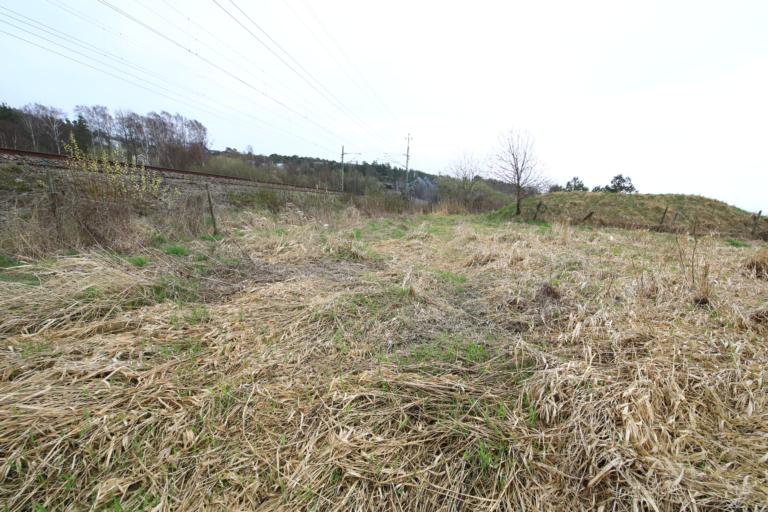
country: SE
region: Halland
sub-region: Kungsbacka Kommun
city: Frillesas
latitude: 57.3071
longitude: 12.1700
